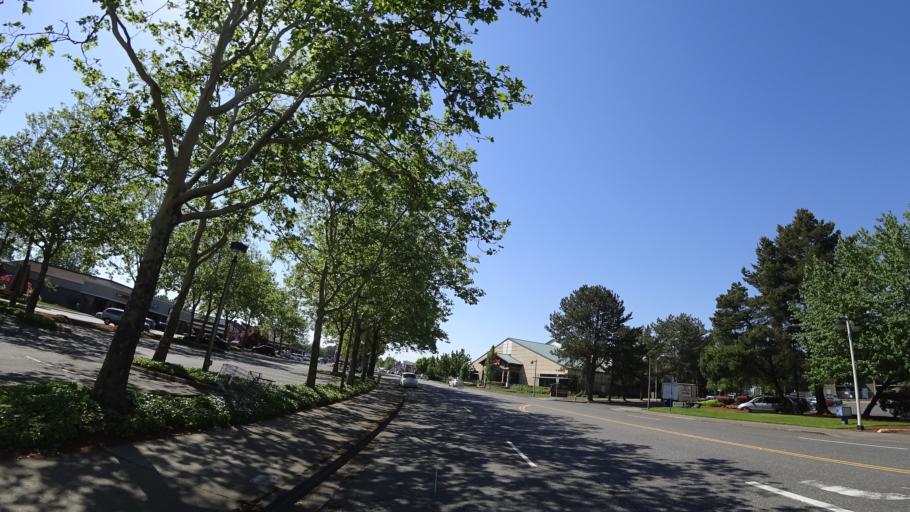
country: US
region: Oregon
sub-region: Washington County
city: Beaverton
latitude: 45.4934
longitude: -122.8074
